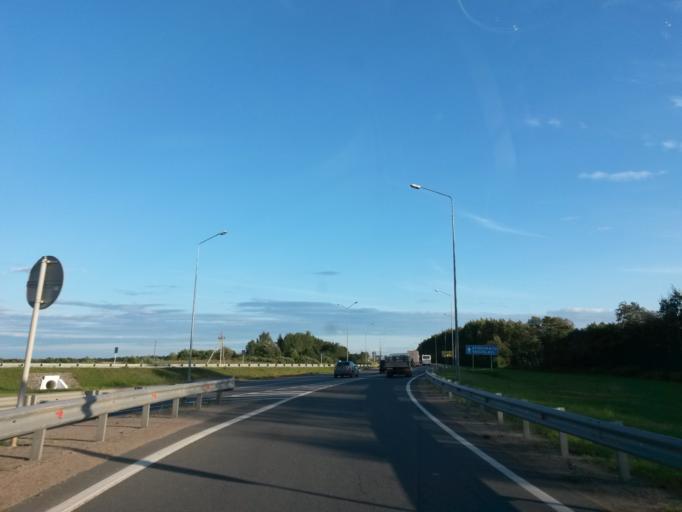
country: RU
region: Jaroslavl
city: Yaroslavl
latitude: 57.7368
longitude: 39.8960
